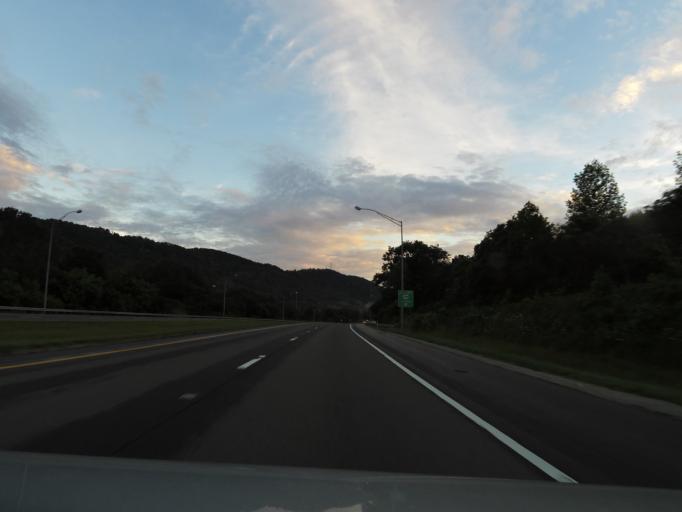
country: US
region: Tennessee
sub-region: Campbell County
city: Jellico
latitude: 36.5838
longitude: -84.1075
